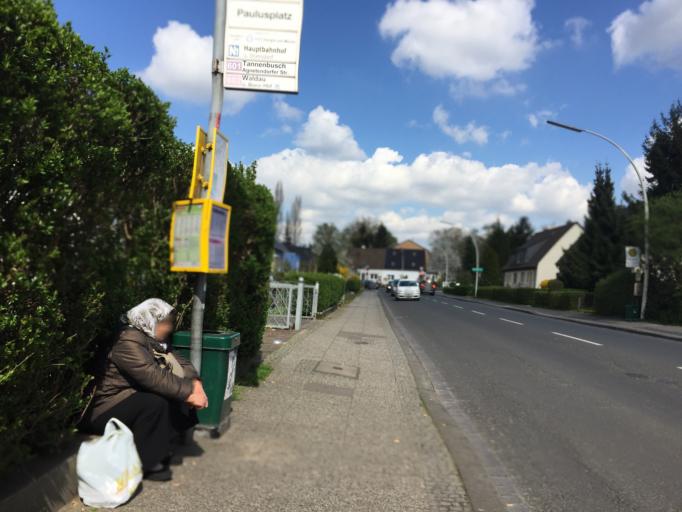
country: DE
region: North Rhine-Westphalia
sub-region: Regierungsbezirk Koln
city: Bonn
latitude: 50.7455
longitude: 7.0659
